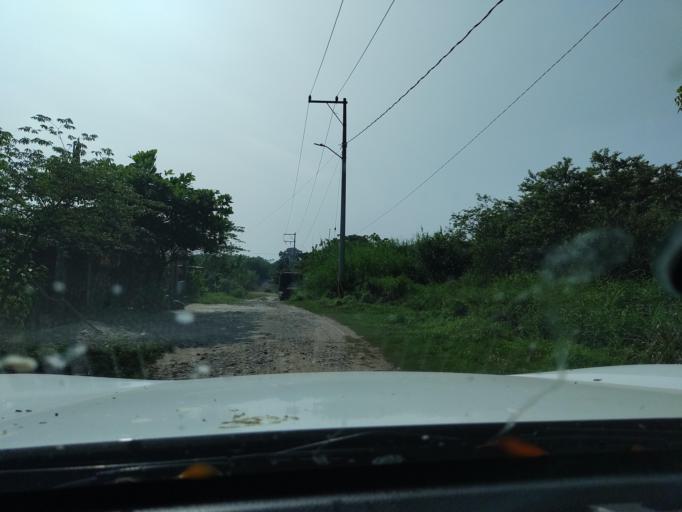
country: MX
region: Veracruz
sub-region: Martinez de la Torre
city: El Progreso
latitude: 20.0761
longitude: -97.0057
